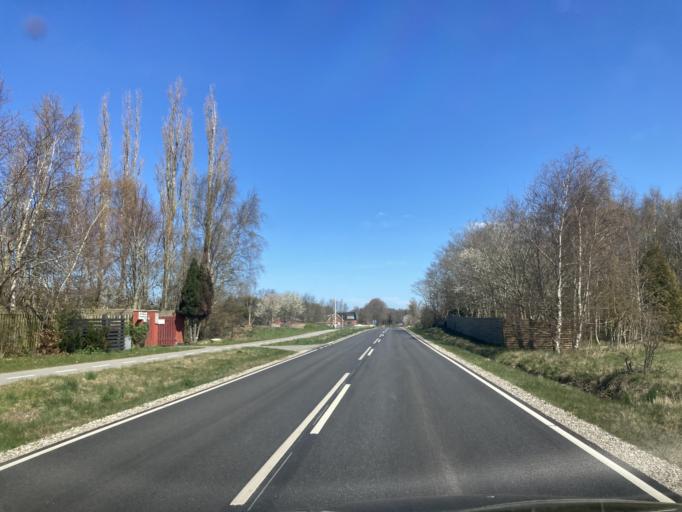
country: DK
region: Capital Region
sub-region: Gribskov Kommune
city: Graested
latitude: 56.1023
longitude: 12.2266
